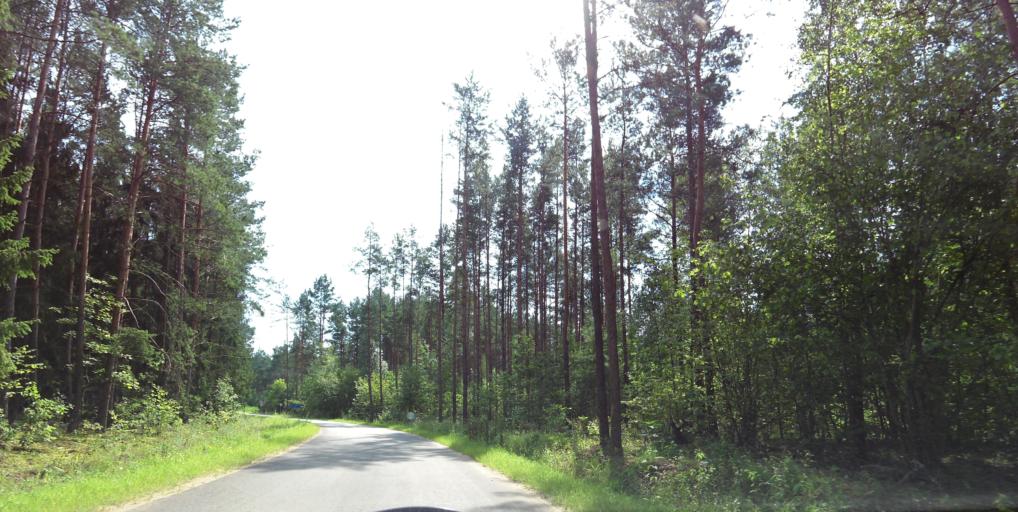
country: LT
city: Grigiskes
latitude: 54.7289
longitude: 25.0447
